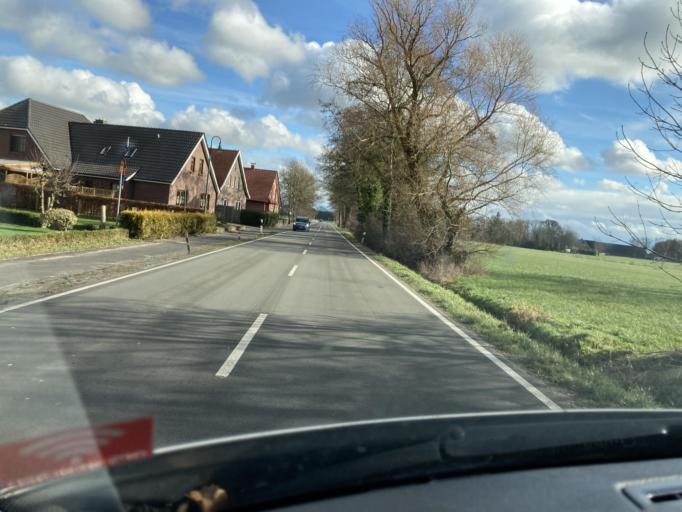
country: DE
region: Lower Saxony
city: Ostrhauderfehn
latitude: 53.1689
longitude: 7.5782
